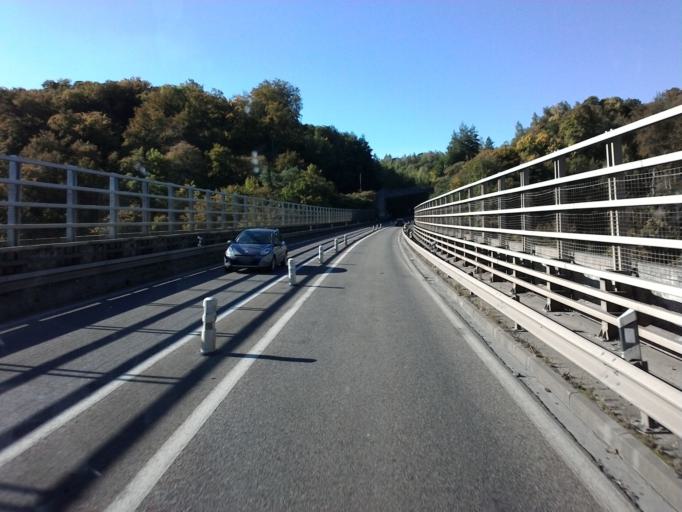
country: FR
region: Lorraine
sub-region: Departement de Meurthe-et-Moselle
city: Rehon
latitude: 49.5069
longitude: 5.7548
